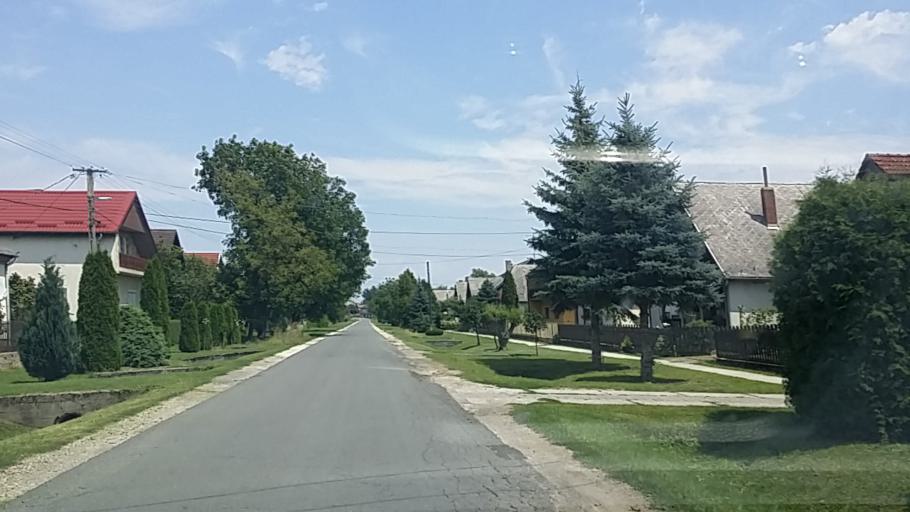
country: HU
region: Zala
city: Murakeresztur
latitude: 46.3601
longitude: 16.8801
